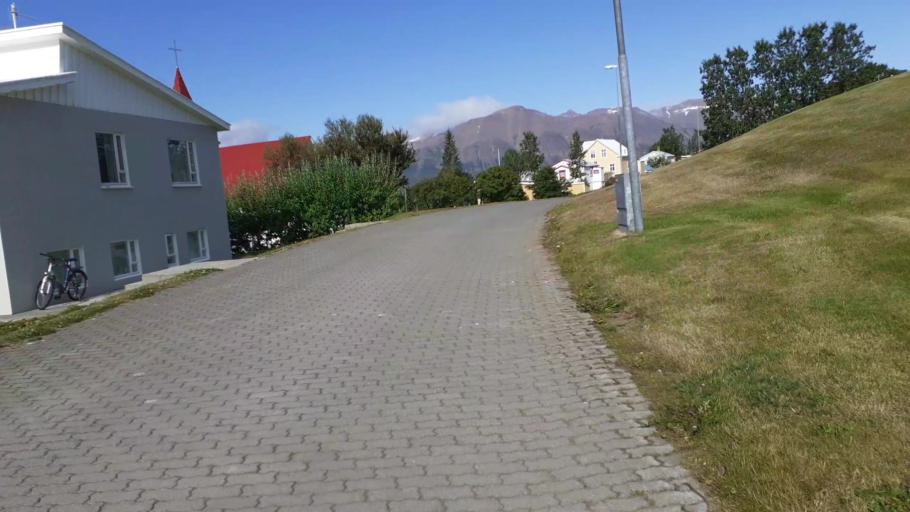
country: IS
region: Northeast
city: Dalvik
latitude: 65.9791
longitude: -18.3739
